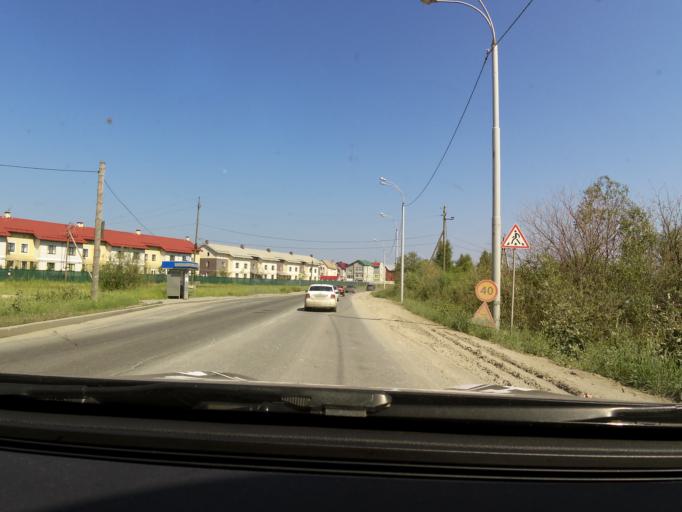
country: RU
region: Sverdlovsk
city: Shirokaya Rechka
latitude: 56.8003
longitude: 60.4945
